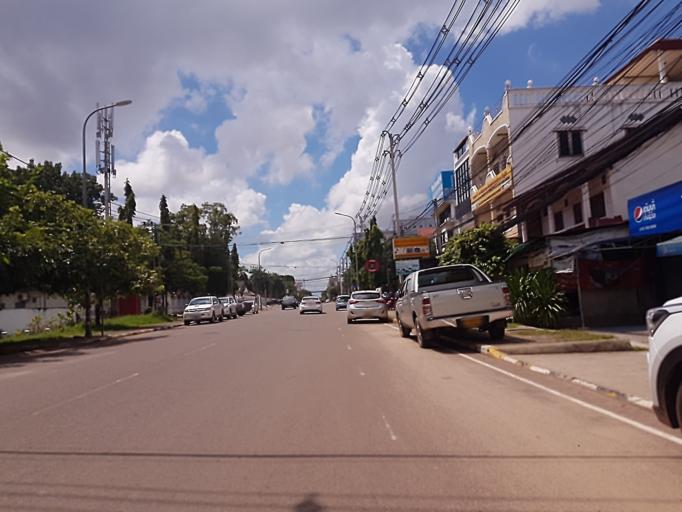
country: LA
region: Vientiane
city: Vientiane
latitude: 17.9734
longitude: 102.6257
